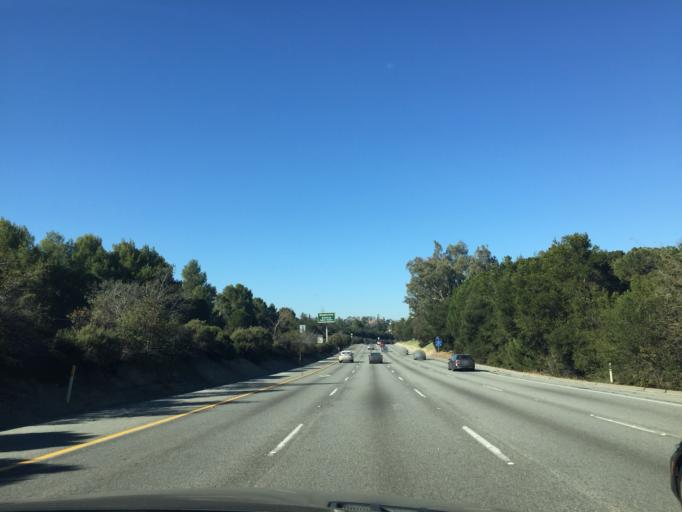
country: US
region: California
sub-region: Santa Clara County
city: Loyola
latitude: 37.3462
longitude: -122.0982
